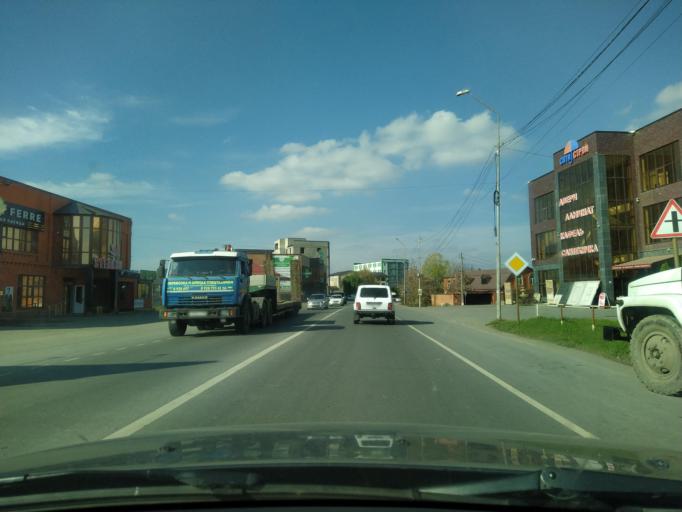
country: RU
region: Ingushetiya
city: Magas
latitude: 43.1976
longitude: 44.7572
